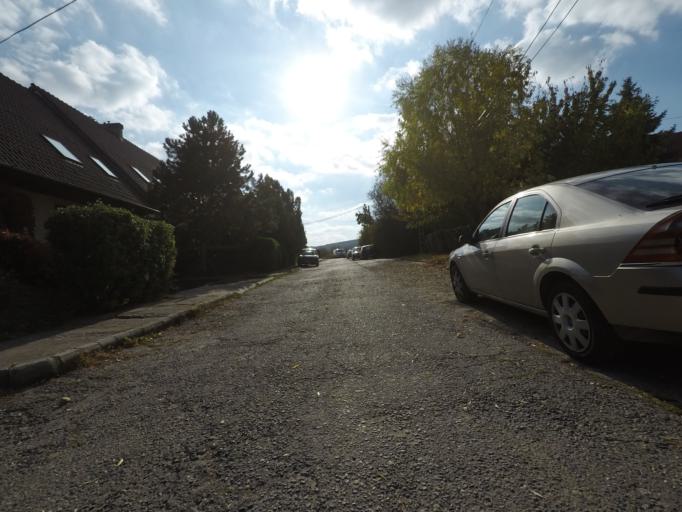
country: HU
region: Pest
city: Pomaz
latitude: 47.6317
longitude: 19.0305
